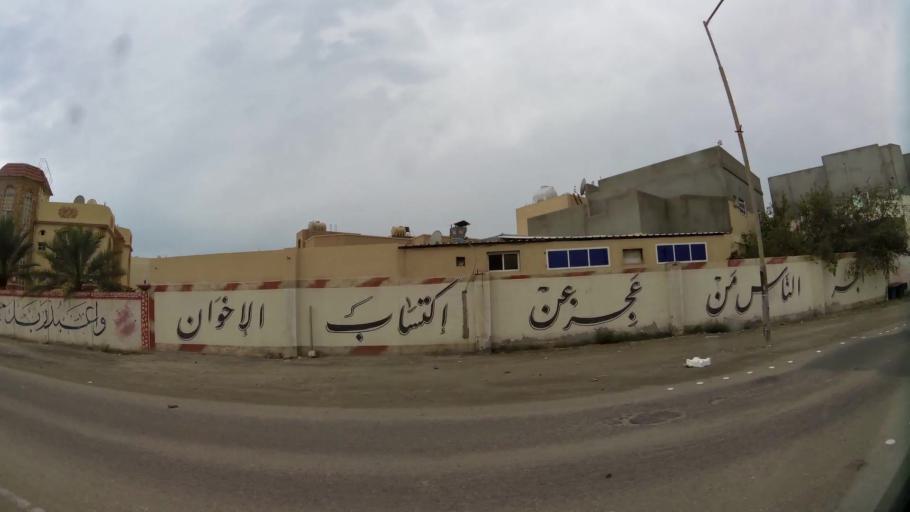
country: BH
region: Central Governorate
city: Madinat Hamad
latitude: 26.1282
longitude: 50.4773
